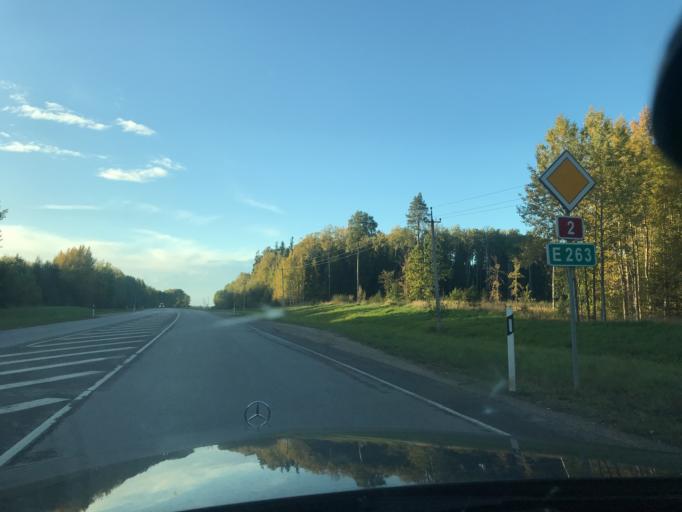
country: EE
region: Vorumaa
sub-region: Voru linn
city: Voru
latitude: 57.8498
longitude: 27.0370
